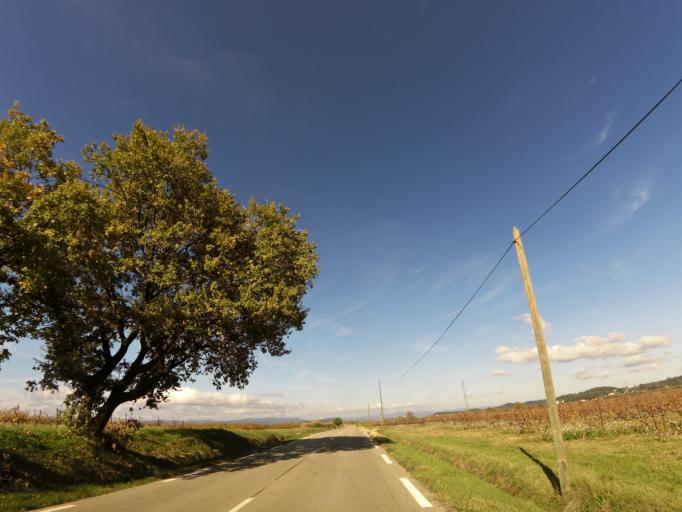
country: FR
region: Languedoc-Roussillon
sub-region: Departement du Gard
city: Ledignan
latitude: 44.0015
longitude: 4.1037
